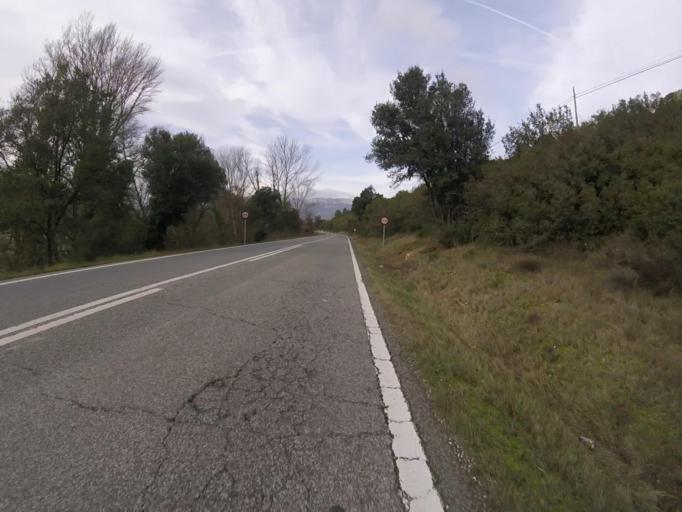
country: ES
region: Navarre
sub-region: Provincia de Navarra
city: Estella
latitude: 42.7023
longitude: -2.0609
